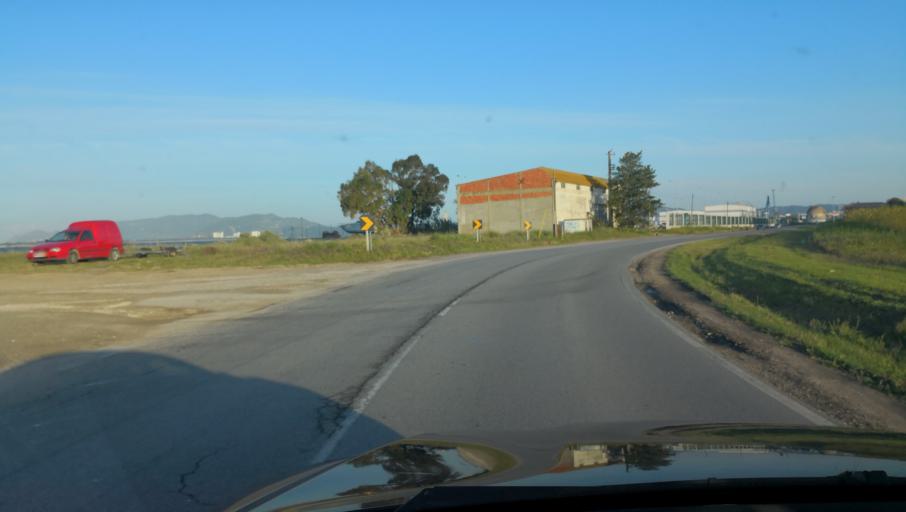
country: PT
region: Setubal
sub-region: Setubal
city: Setubal
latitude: 38.4939
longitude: -8.8313
